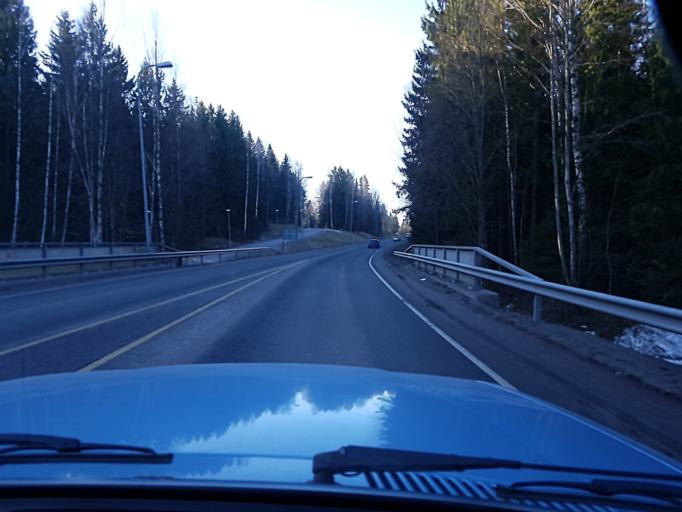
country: FI
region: Uusimaa
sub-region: Helsinki
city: Kilo
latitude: 60.2806
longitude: 24.8361
